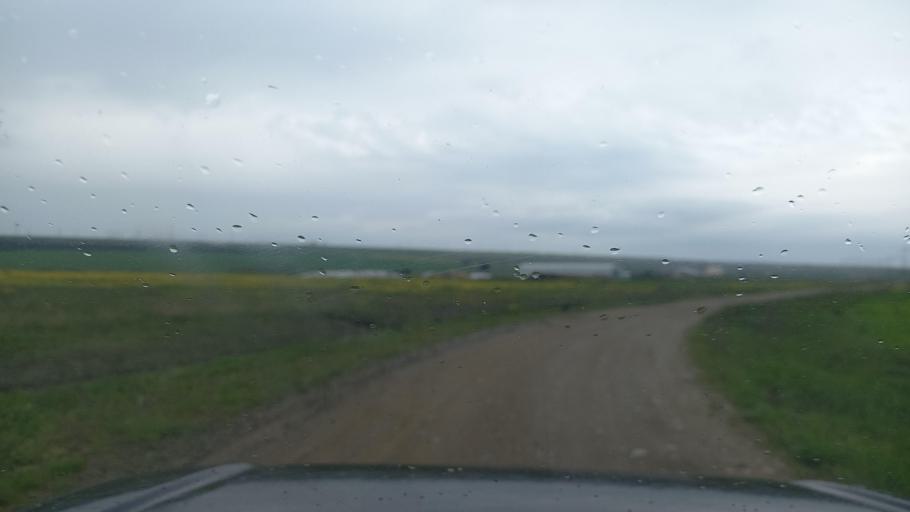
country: RU
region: Stavropol'skiy
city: Kursavka
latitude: 44.5990
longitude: 42.2487
